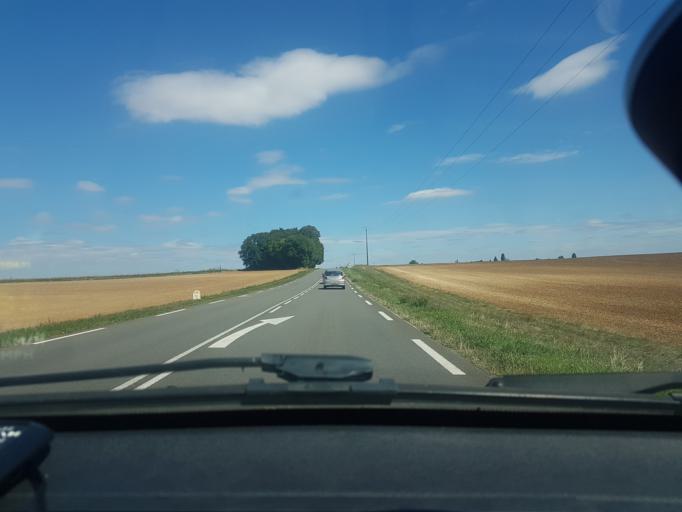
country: FR
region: Bourgogne
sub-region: Departement de la Cote-d'Or
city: Belleneuve
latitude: 47.3767
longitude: 5.2371
